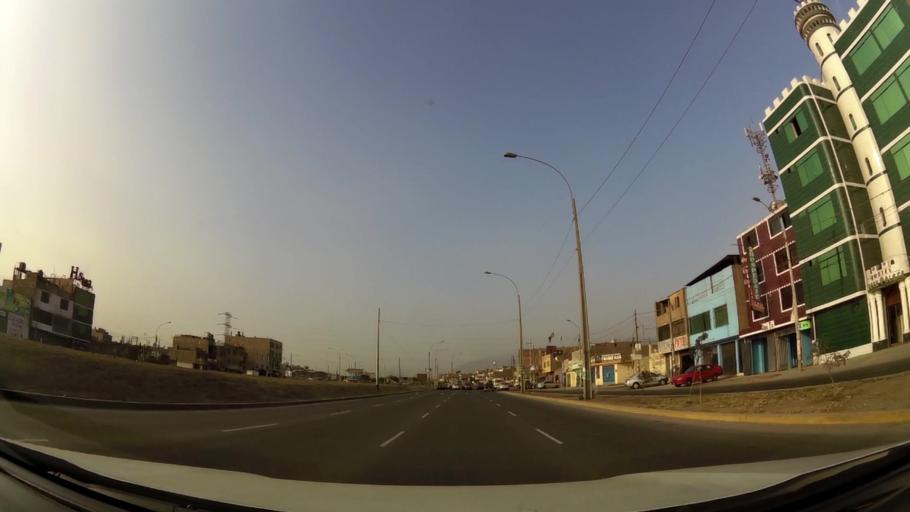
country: PE
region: Lima
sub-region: Lima
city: Independencia
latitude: -11.9752
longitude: -77.0894
